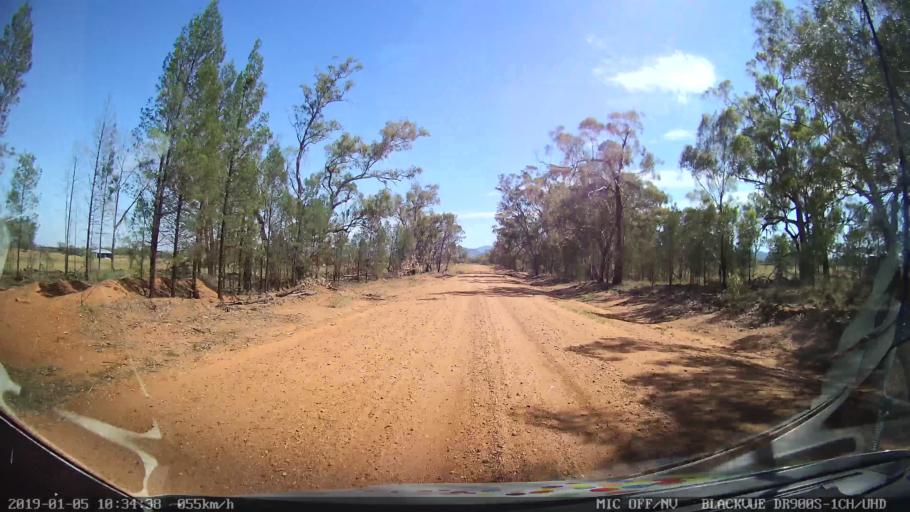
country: AU
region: New South Wales
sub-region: Gilgandra
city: Gilgandra
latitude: -31.4968
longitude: 148.9292
